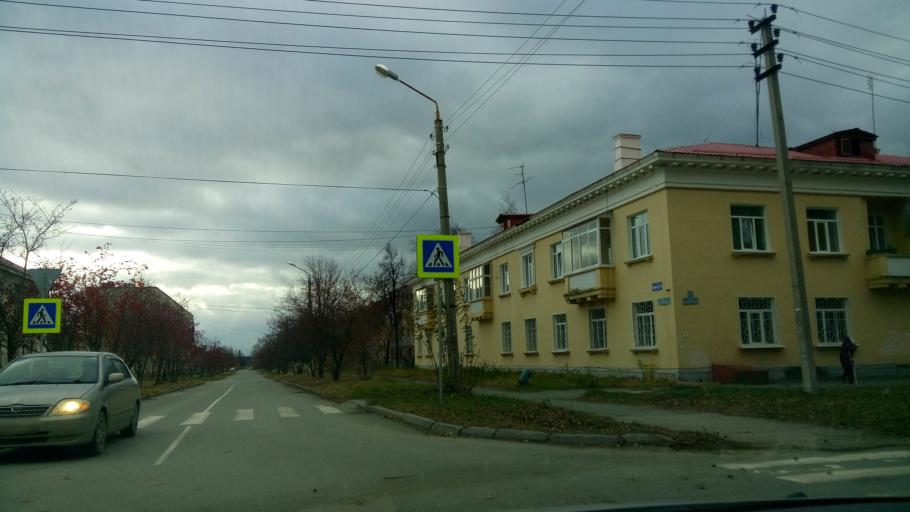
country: RU
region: Sverdlovsk
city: Sredneuralsk
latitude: 56.9869
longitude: 60.4672
